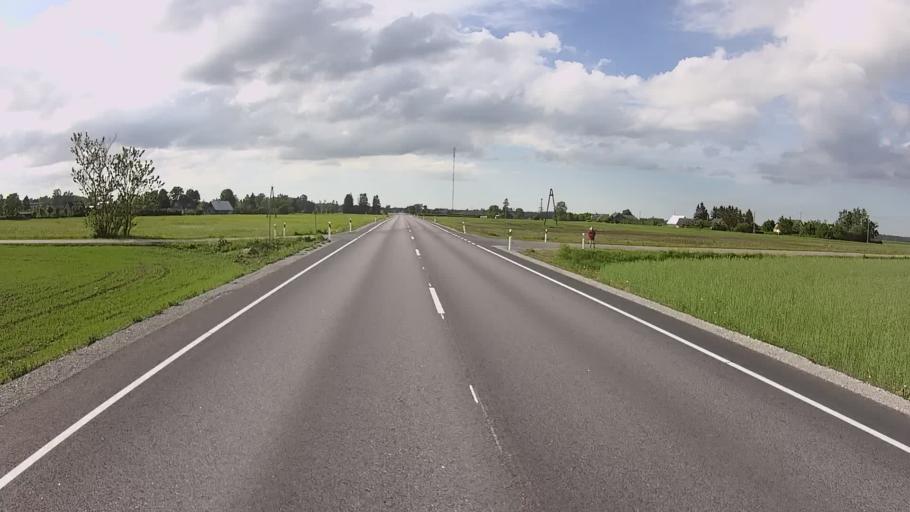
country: EE
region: Laeaene-Virumaa
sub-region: Vinni vald
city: Vinni
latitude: 59.2446
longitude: 26.4812
